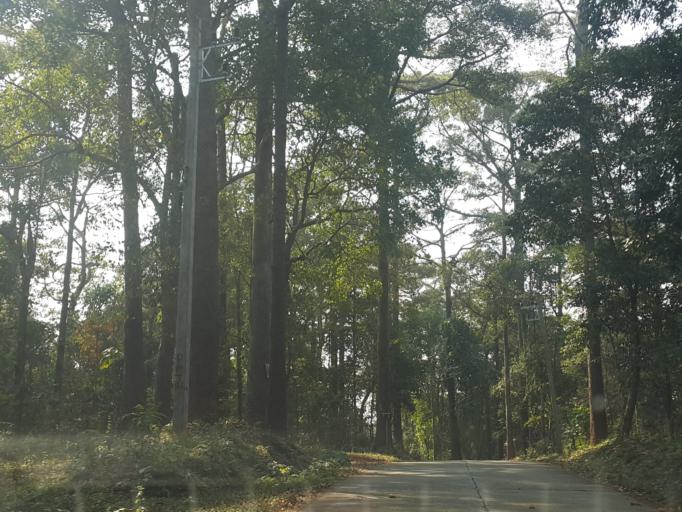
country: TH
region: Chiang Mai
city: Mae Taeng
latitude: 19.0235
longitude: 98.7912
